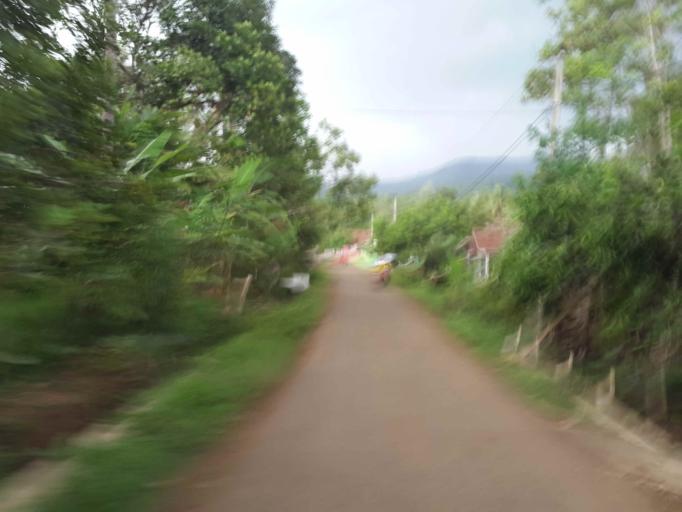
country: ID
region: Central Java
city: Limbangan
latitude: -7.2964
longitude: 108.7048
